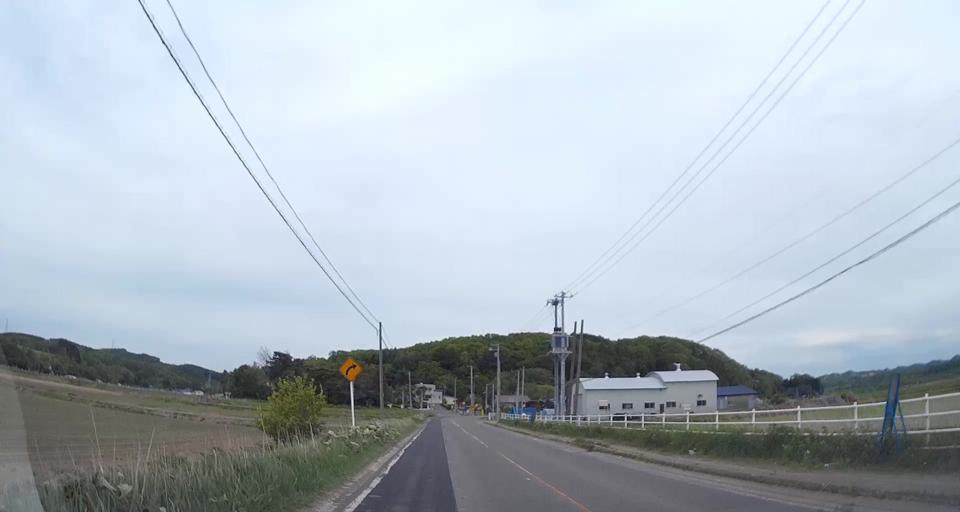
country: JP
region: Hokkaido
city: Chitose
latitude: 42.7355
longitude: 141.8917
